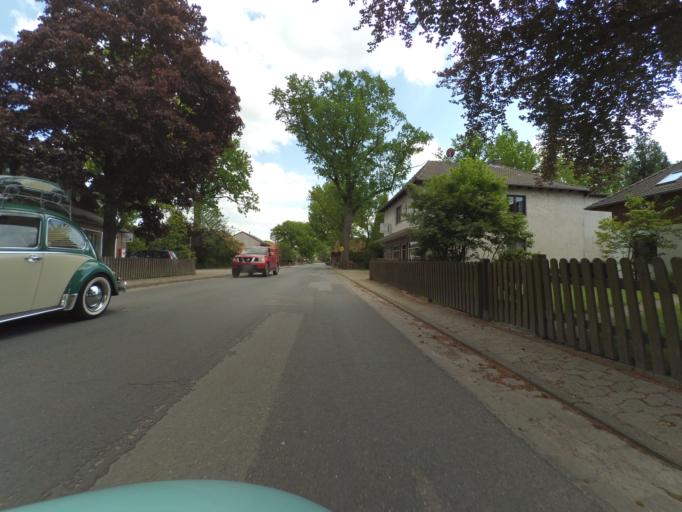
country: DE
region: Lower Saxony
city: Muden
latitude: 52.5250
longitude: 10.3640
